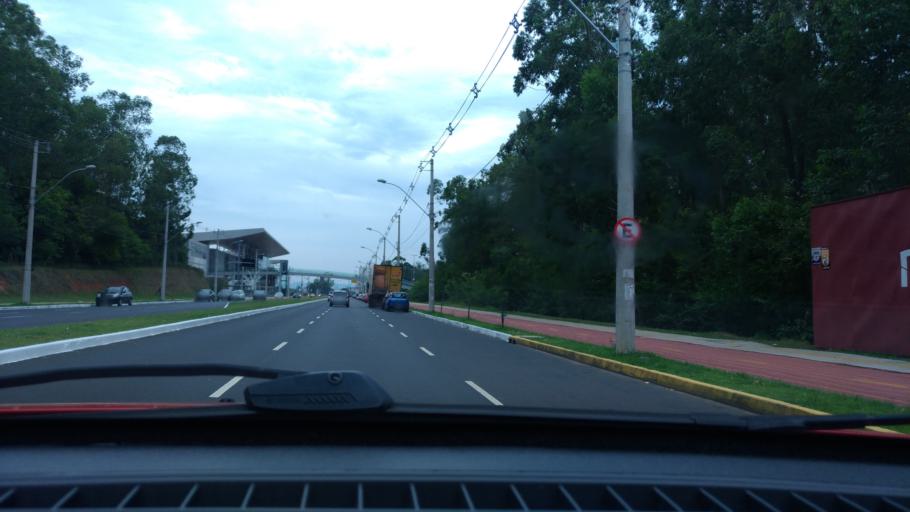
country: BR
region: Rio Grande do Sul
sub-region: Canoas
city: Canoas
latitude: -29.9090
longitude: -51.1654
